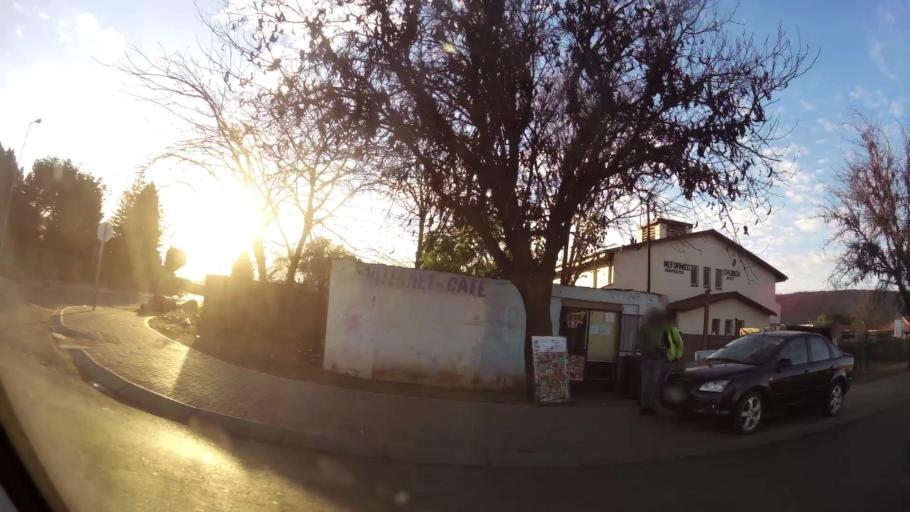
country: ZA
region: Gauteng
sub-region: City of Tshwane Metropolitan Municipality
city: Cullinan
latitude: -25.7109
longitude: 28.3596
